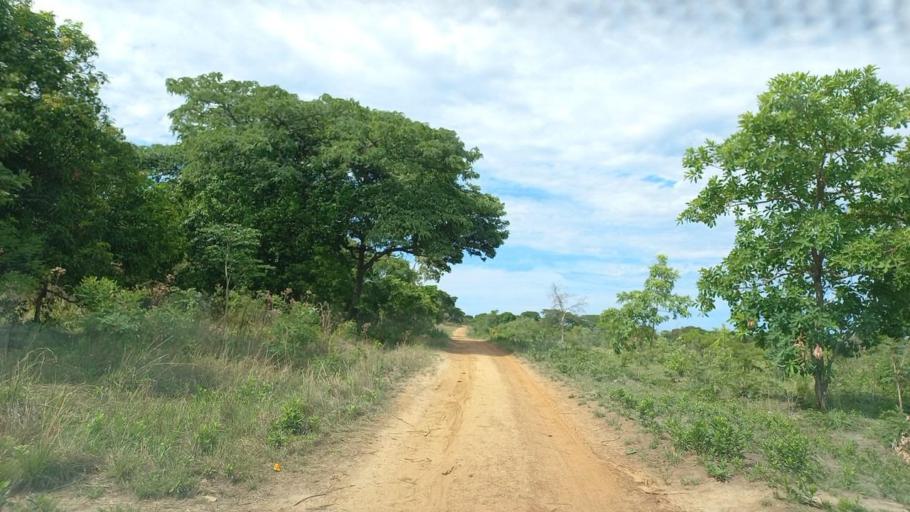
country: ZM
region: North-Western
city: Kabompo
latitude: -13.5109
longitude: 24.3936
